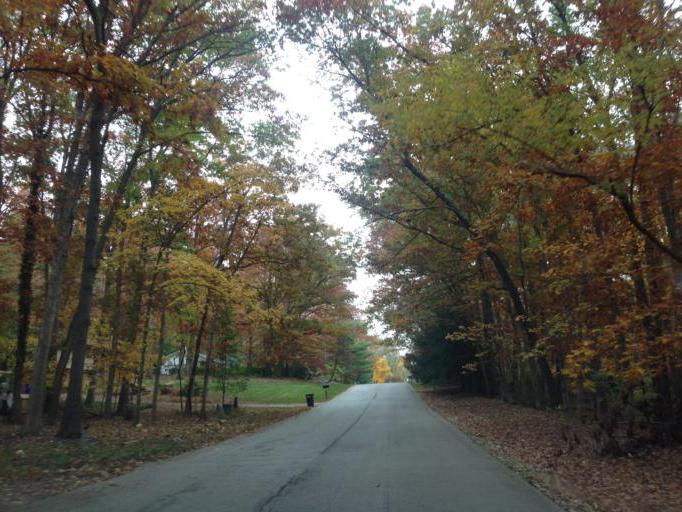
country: US
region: Maryland
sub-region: Howard County
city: Highland
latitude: 39.2715
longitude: -76.9408
